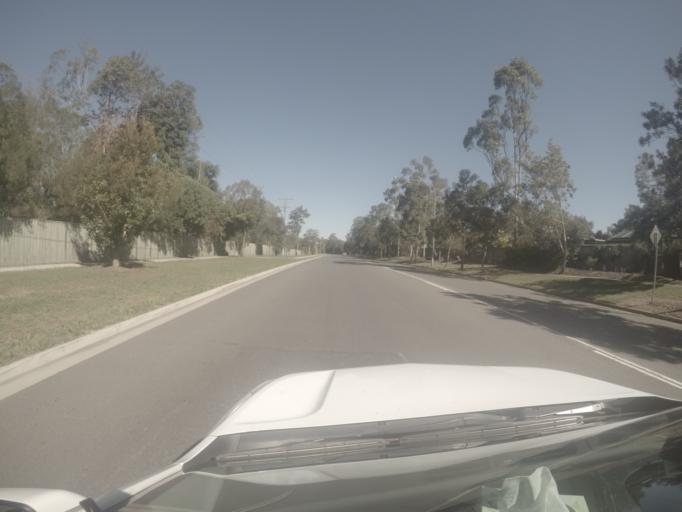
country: AU
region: Queensland
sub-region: Ipswich
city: Springfield
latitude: -27.6448
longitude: 152.9191
